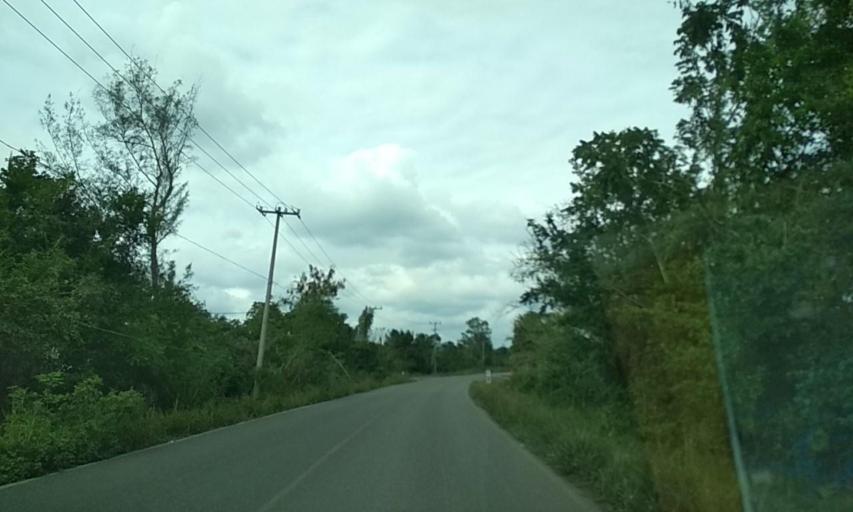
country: MX
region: Veracruz
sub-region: Papantla
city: El Chote
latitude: 20.3815
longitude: -97.3365
